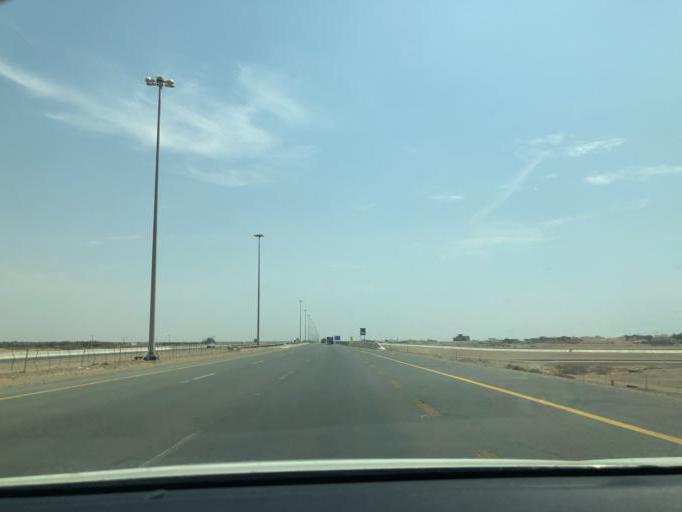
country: SA
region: Makkah
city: Rabigh
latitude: 22.2699
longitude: 39.1236
